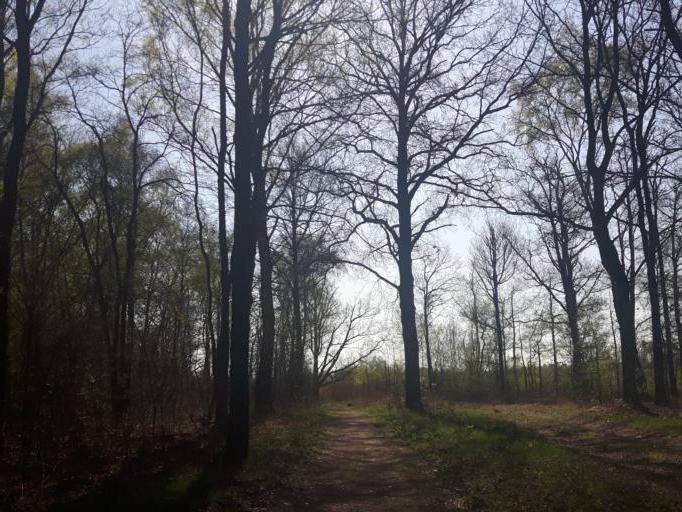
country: NL
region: Overijssel
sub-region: Gemeente Haaksbergen
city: Haaksbergen
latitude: 52.1238
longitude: 6.7706
